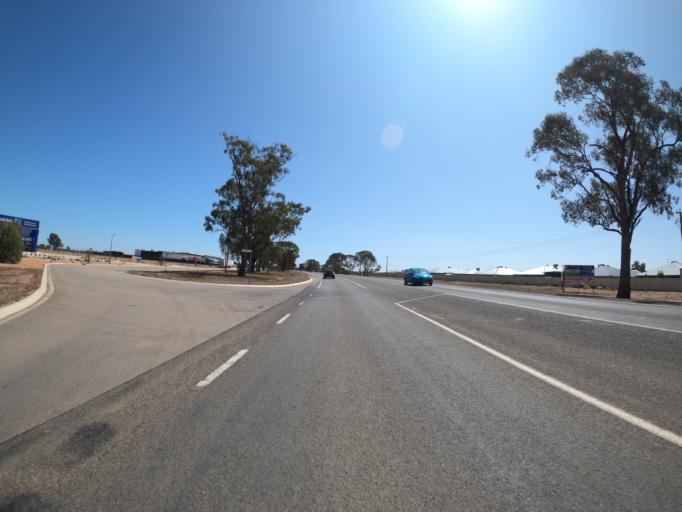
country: AU
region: Victoria
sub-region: Moira
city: Yarrawonga
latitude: -36.0104
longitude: 146.0290
